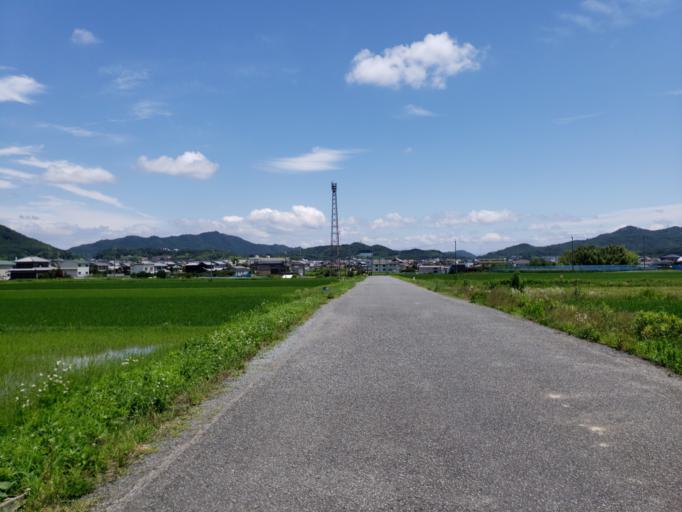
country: JP
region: Hyogo
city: Kakogawacho-honmachi
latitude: 34.8154
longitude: 134.8109
